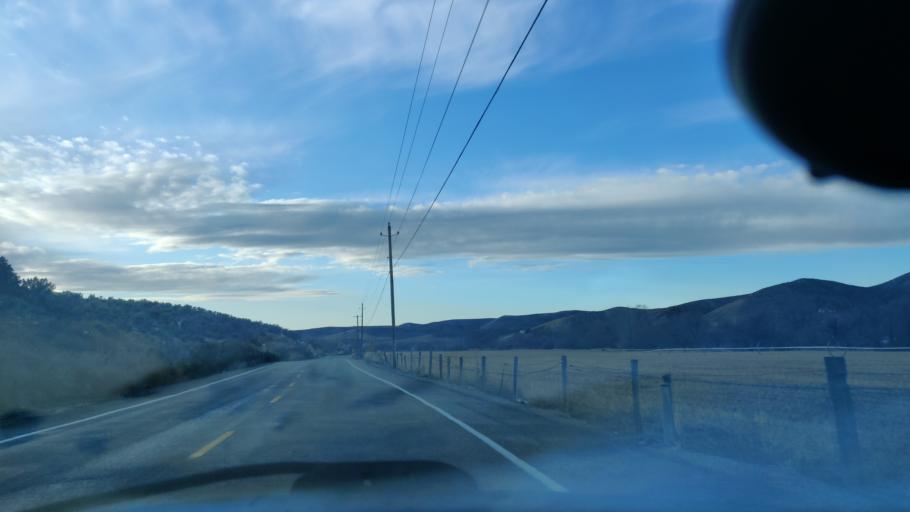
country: US
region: Idaho
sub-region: Ada County
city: Eagle
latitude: 43.7298
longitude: -116.2924
